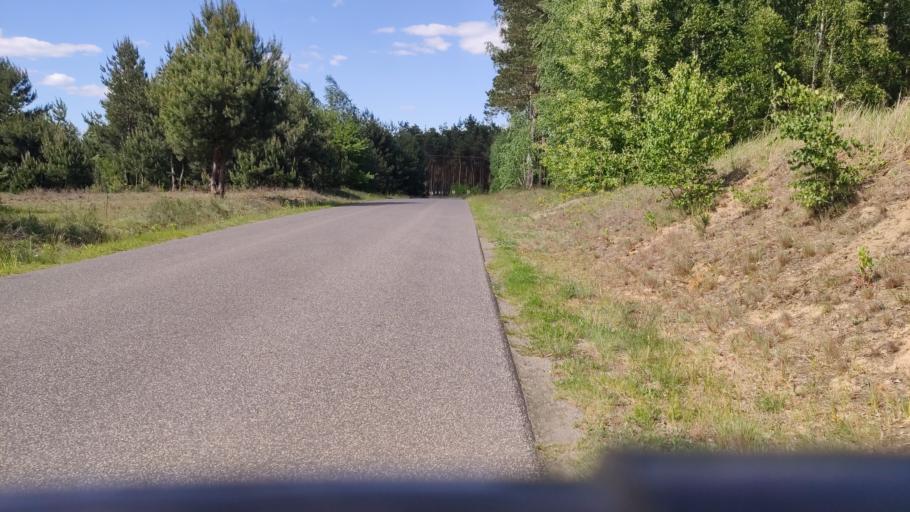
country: PL
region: Kujawsko-Pomorskie
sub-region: Wloclawek
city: Wloclawek
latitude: 52.5886
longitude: 19.0933
